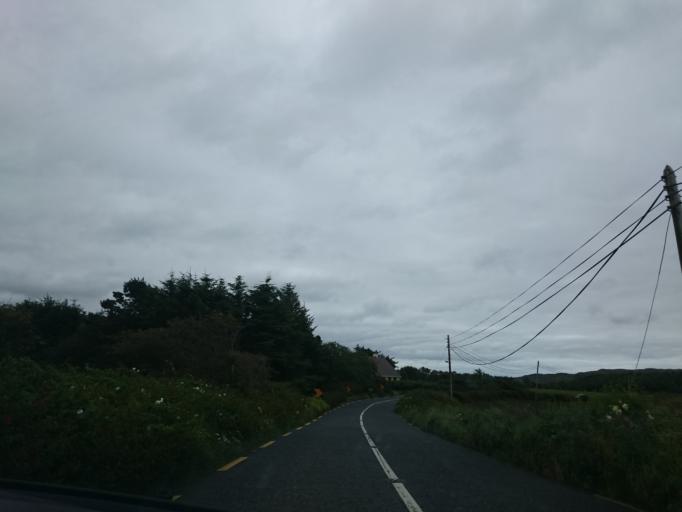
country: IE
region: Connaught
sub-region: County Galway
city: Clifden
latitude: 53.5193
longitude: -10.0410
